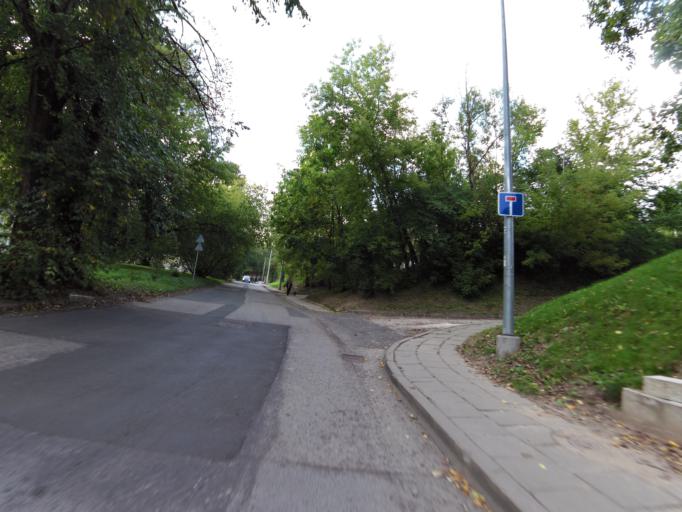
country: LT
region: Vilnius County
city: Seskine
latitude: 54.7022
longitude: 25.2506
